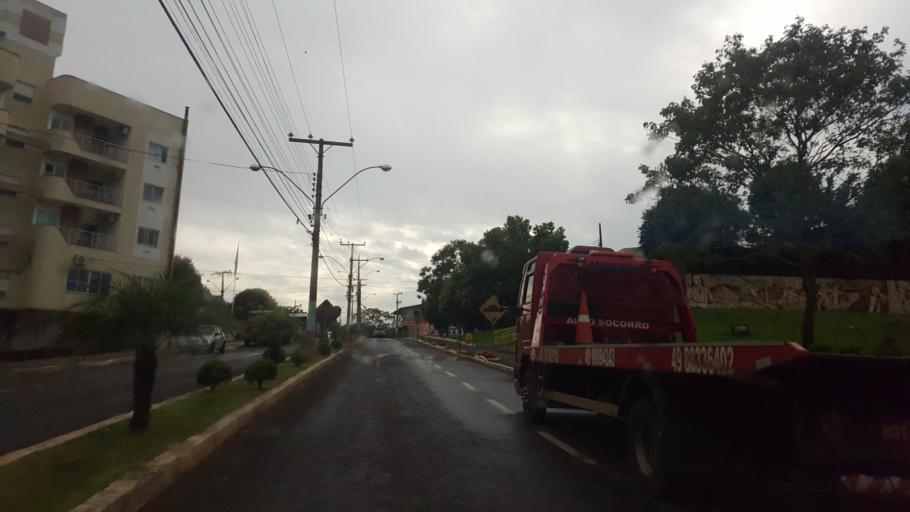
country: BR
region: Rio Grande do Sul
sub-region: Frederico Westphalen
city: Frederico Westphalen
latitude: -27.1019
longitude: -53.3966
